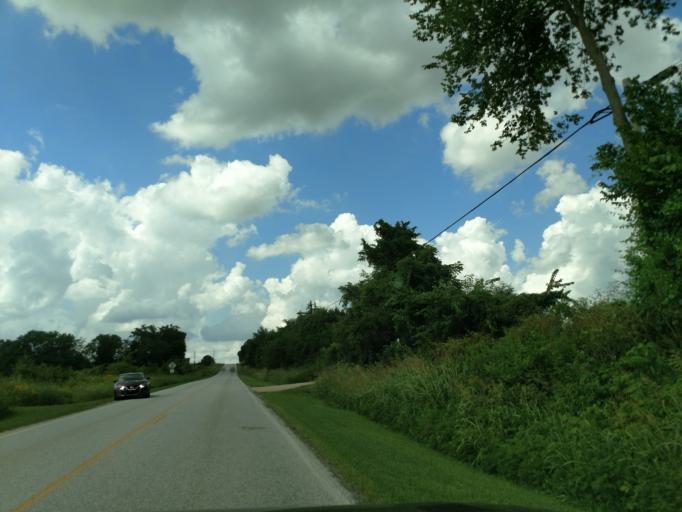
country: US
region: Arkansas
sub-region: Carroll County
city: Berryville
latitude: 36.4094
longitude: -93.5613
